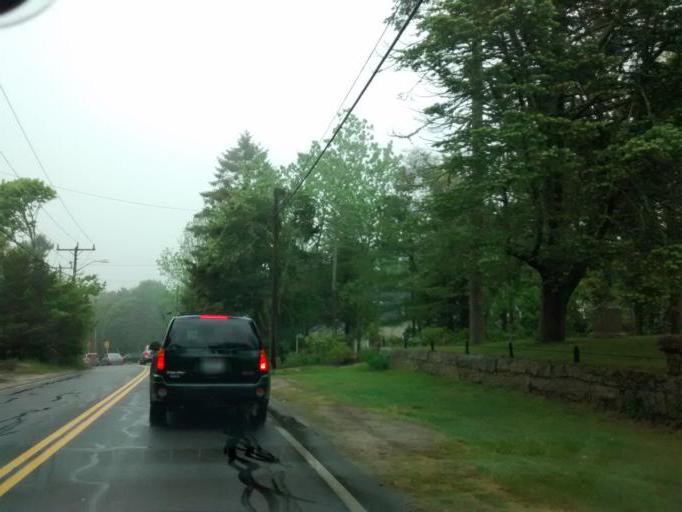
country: US
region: Massachusetts
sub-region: Barnstable County
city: Pocasset
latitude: 41.6948
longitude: -70.6050
